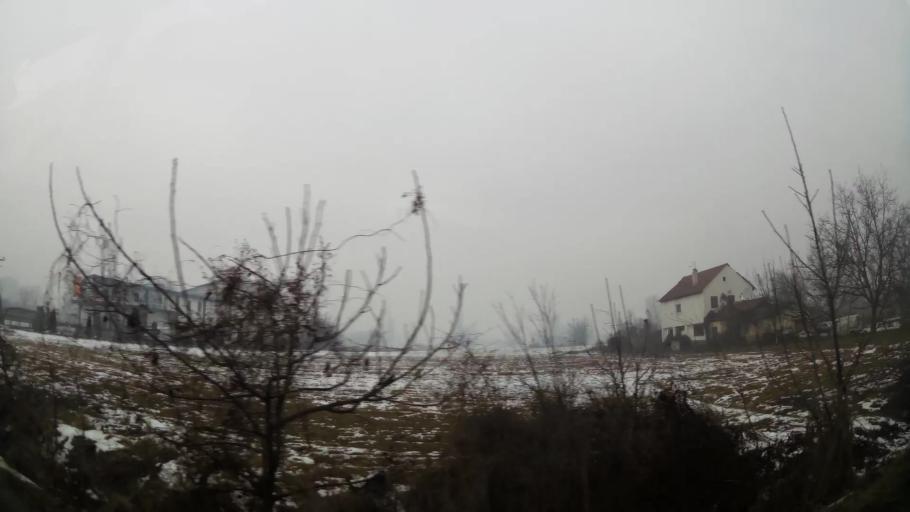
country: MK
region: Ilinden
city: Idrizovo
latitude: 41.9568
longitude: 21.5819
